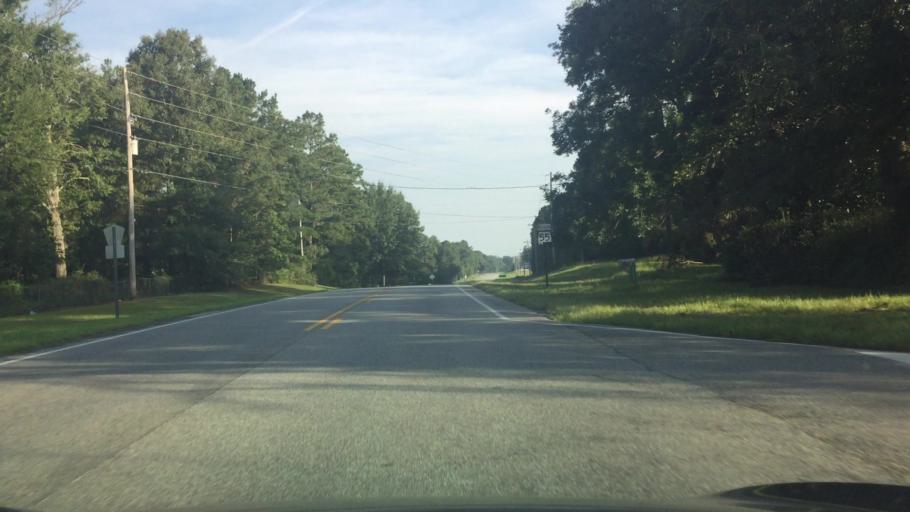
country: US
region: Alabama
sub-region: Covington County
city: Andalusia
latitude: 31.2601
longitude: -86.4705
